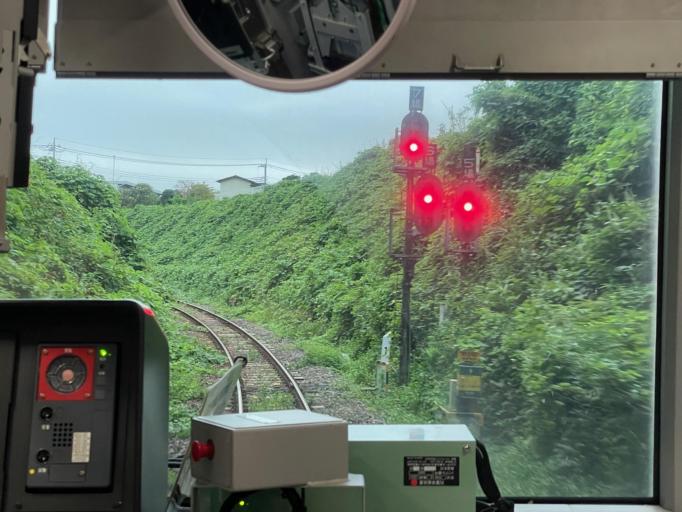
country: JP
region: Tochigi
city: Ujiie
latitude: 36.6391
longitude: 139.9806
